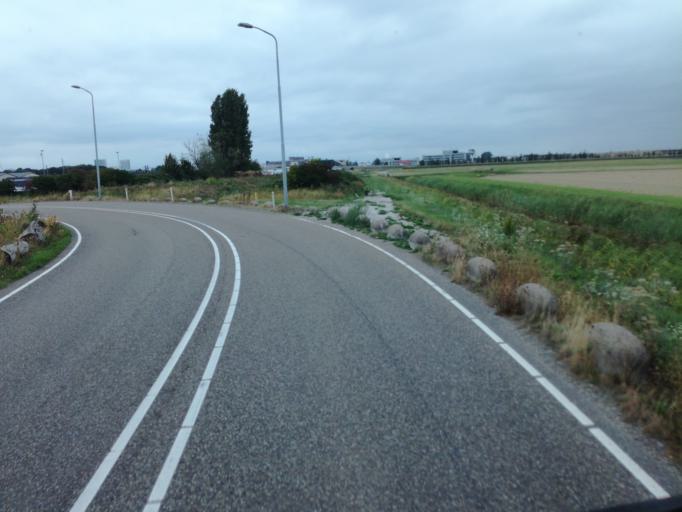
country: NL
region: North Holland
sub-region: Gemeente Aalsmeer
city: Aalsmeer
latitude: 52.2850
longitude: 4.7362
